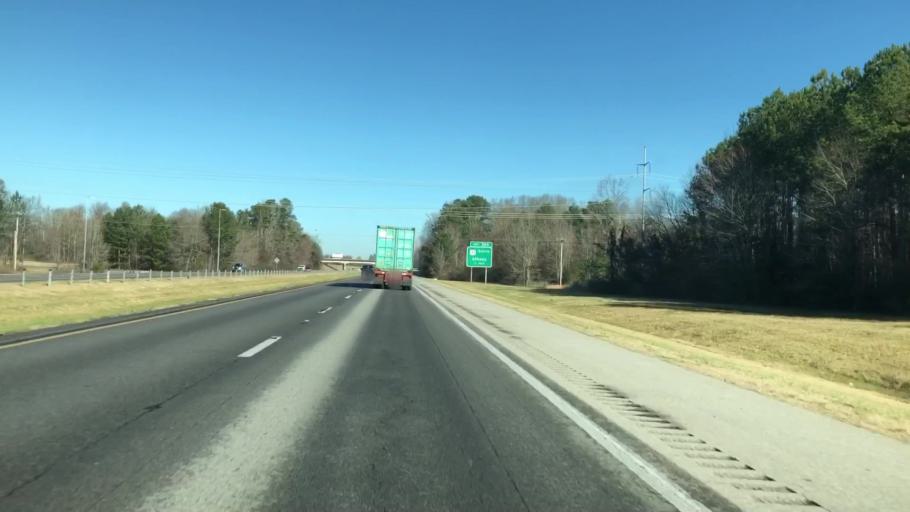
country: US
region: Alabama
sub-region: Limestone County
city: Athens
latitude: 34.8227
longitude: -86.9387
